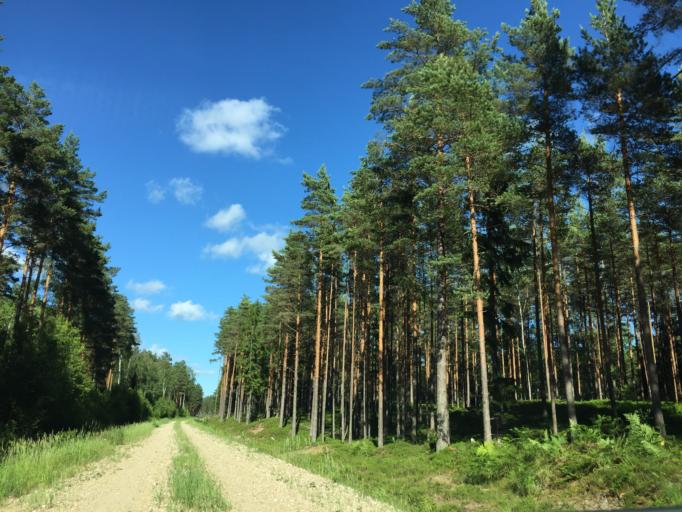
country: LV
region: Ventspils
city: Ventspils
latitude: 57.5407
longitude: 21.7509
